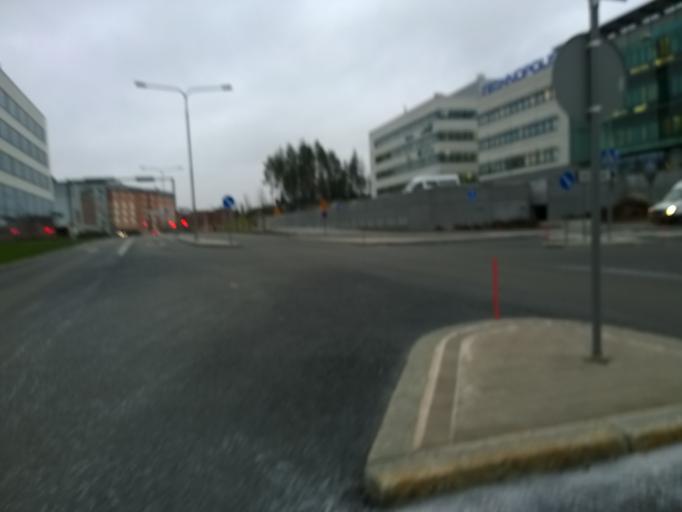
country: FI
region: Pirkanmaa
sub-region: Tampere
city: Tampere
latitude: 61.4467
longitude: 23.8560
